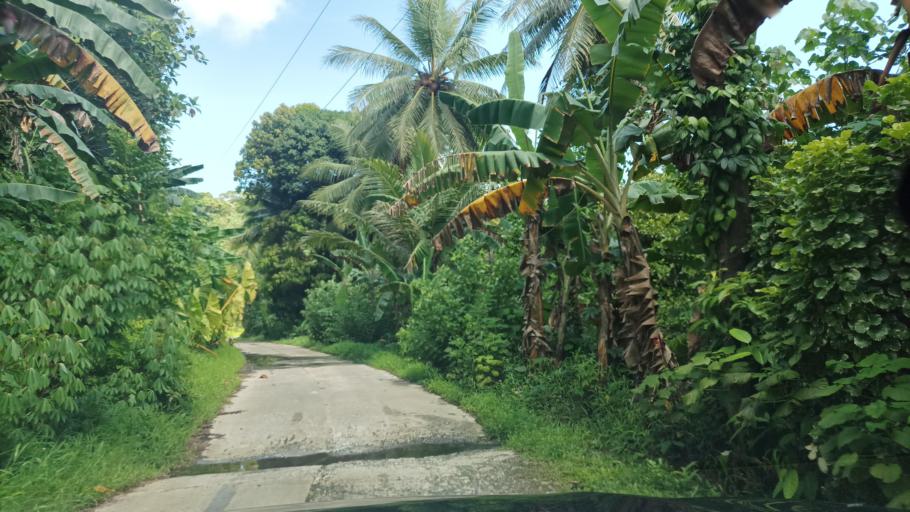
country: FM
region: Pohnpei
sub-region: Sokehs Municipality
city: Palikir - National Government Center
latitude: 6.9412
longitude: 158.1655
